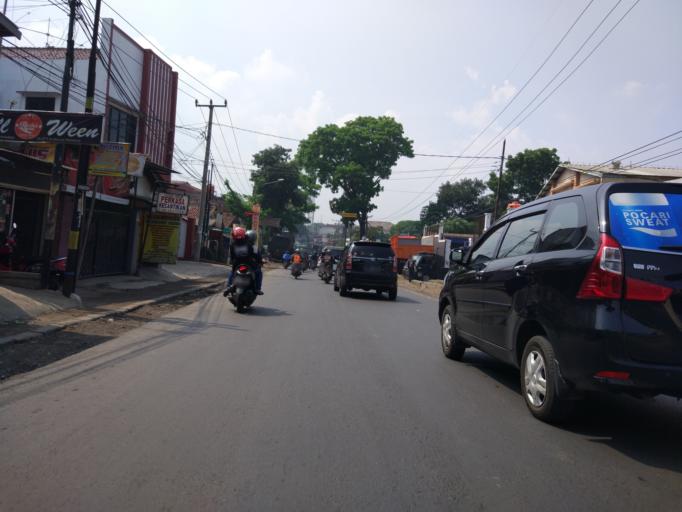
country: ID
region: West Java
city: Cileunyi
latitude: -6.9399
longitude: 107.7402
